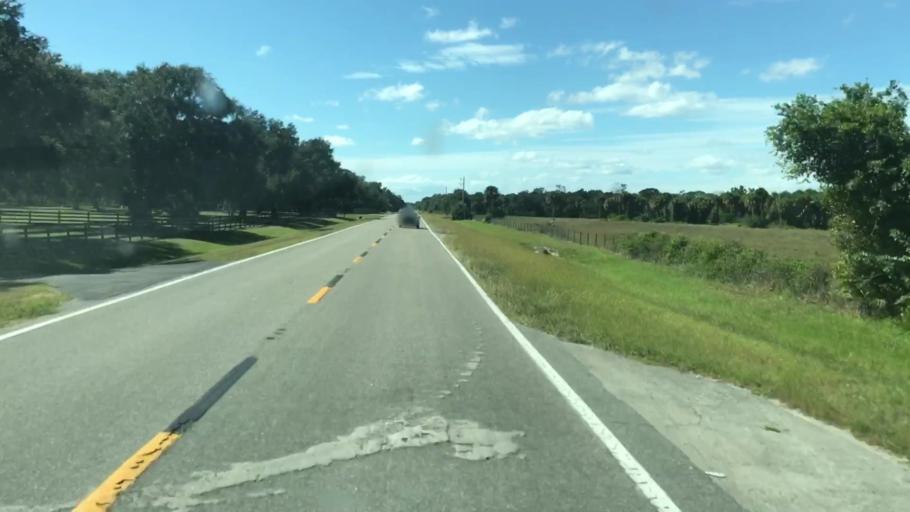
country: US
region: Florida
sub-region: Lee County
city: Olga
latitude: 26.7400
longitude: -81.7288
